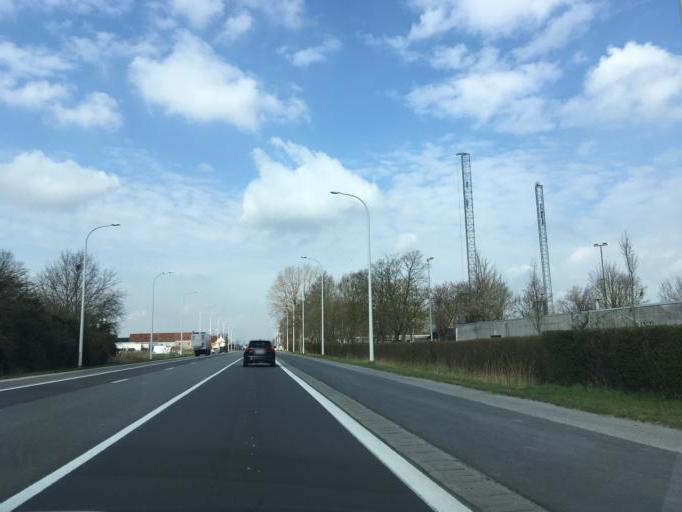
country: BE
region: Flanders
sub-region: Provincie West-Vlaanderen
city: Izegem
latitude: 50.9108
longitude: 3.2051
